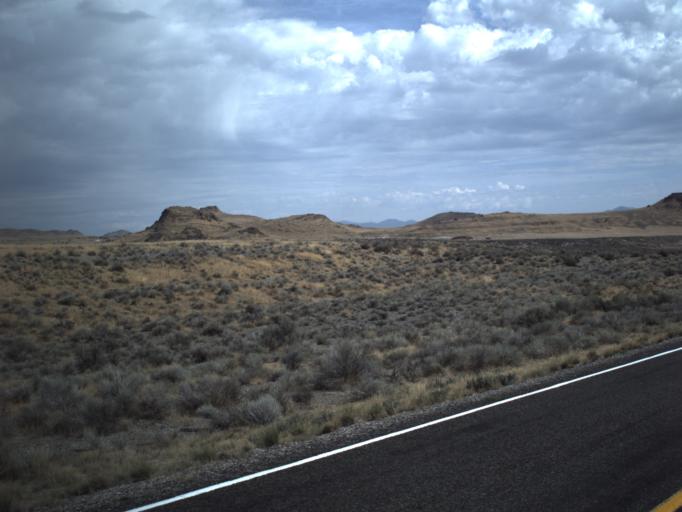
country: US
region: Nevada
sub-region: Elko County
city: West Wendover
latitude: 41.3710
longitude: -114.0300
